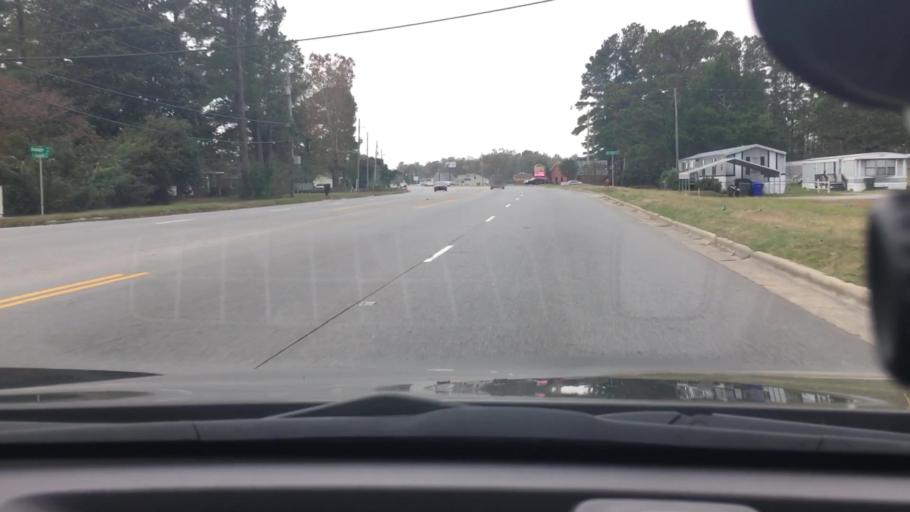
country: US
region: North Carolina
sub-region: Pitt County
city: Summerfield
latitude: 35.5741
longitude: -77.4160
